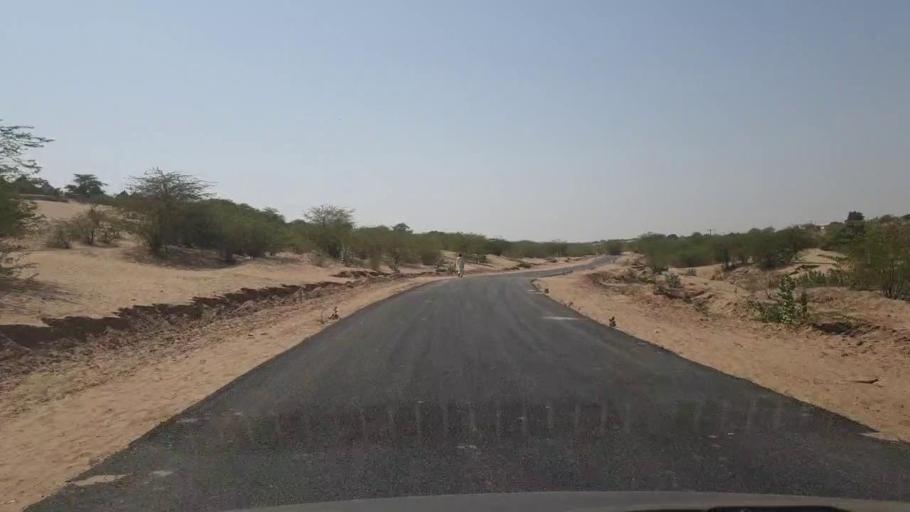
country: PK
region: Sindh
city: Chor
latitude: 25.5662
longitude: 70.1768
